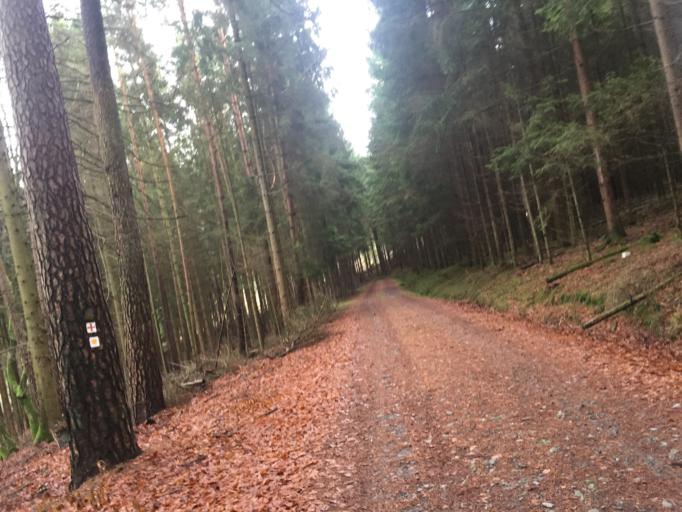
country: DE
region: Hesse
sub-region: Regierungsbezirk Darmstadt
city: Frankisch-Crumbach
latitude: 49.7112
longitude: 8.9118
